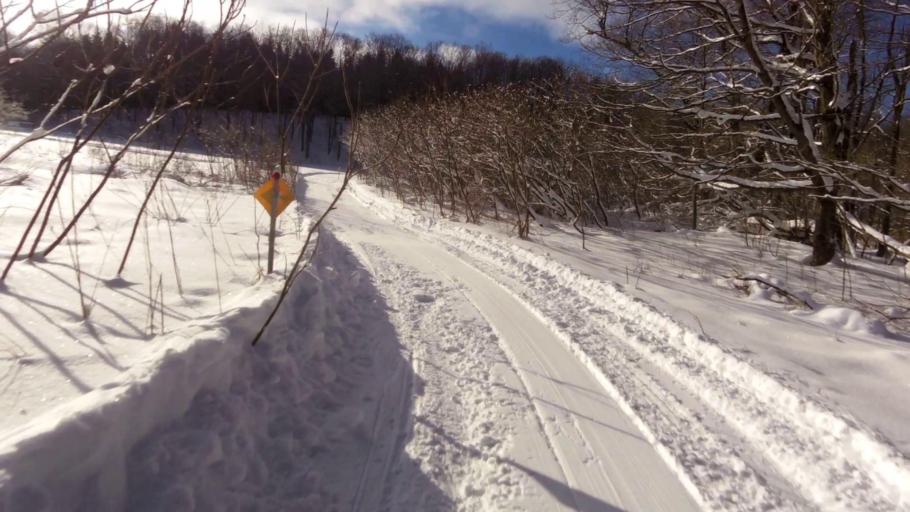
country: US
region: New York
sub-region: Chautauqua County
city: Falconer
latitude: 42.2543
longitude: -79.1514
